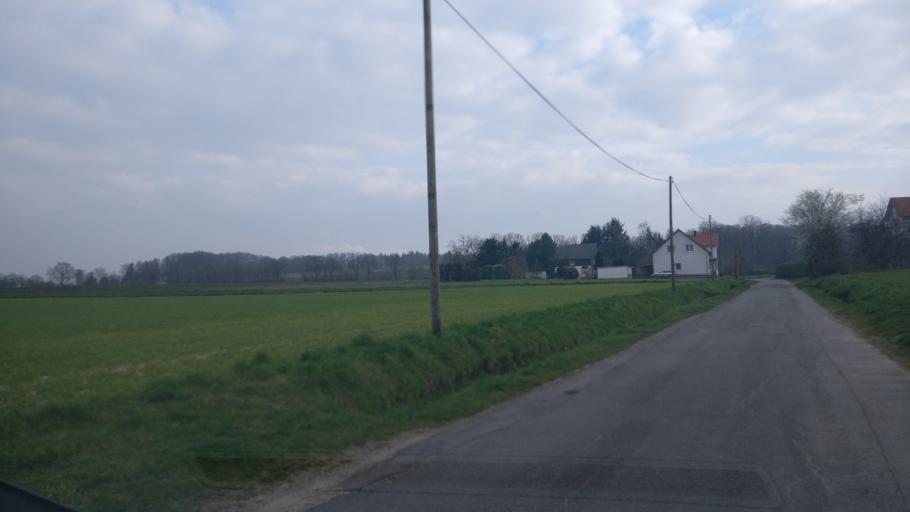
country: DE
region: North Rhine-Westphalia
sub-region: Regierungsbezirk Detmold
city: Lage
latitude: 52.0101
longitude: 8.7841
